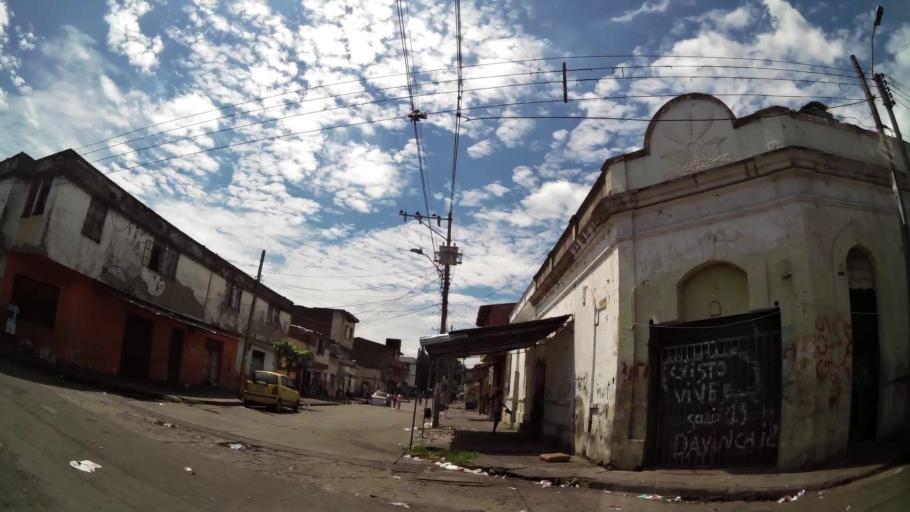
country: CO
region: Valle del Cauca
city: Cali
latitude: 3.4458
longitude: -76.5284
